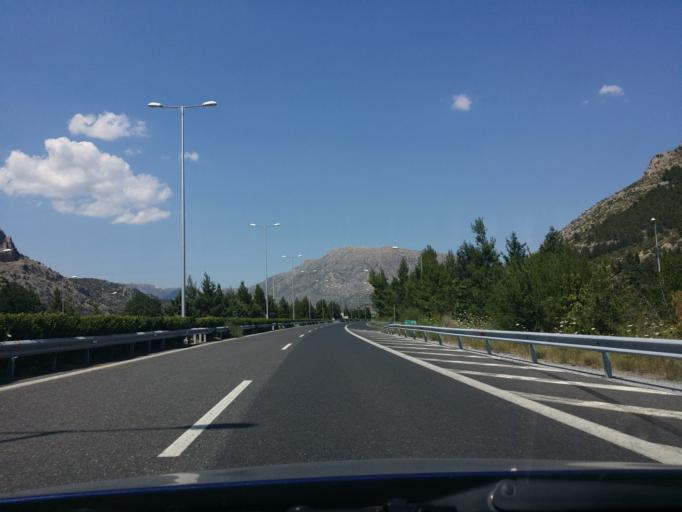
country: GR
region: Peloponnese
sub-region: Nomos Arkadias
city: Tripoli
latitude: 37.5896
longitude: 22.4359
